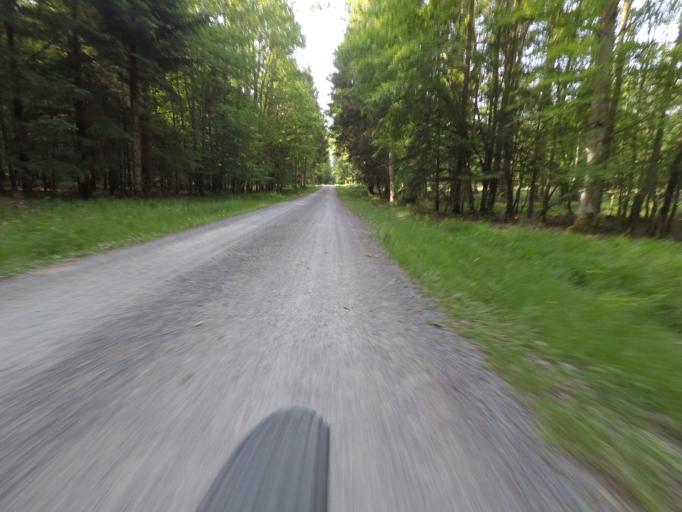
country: DE
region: Baden-Wuerttemberg
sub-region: Regierungsbezirk Stuttgart
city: Weil im Schonbuch
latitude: 48.5818
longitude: 9.0586
